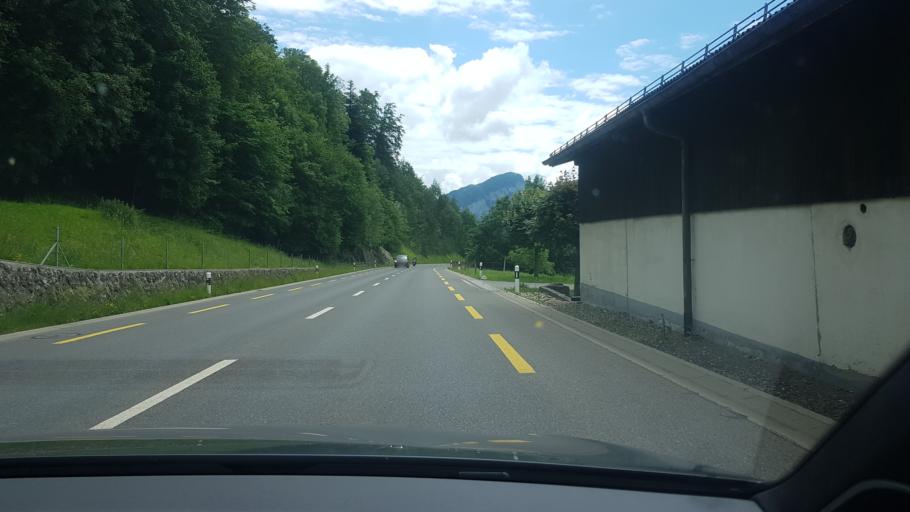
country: CH
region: Schwyz
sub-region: Bezirk Schwyz
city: Steinen
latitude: 47.0613
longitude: 8.6214
